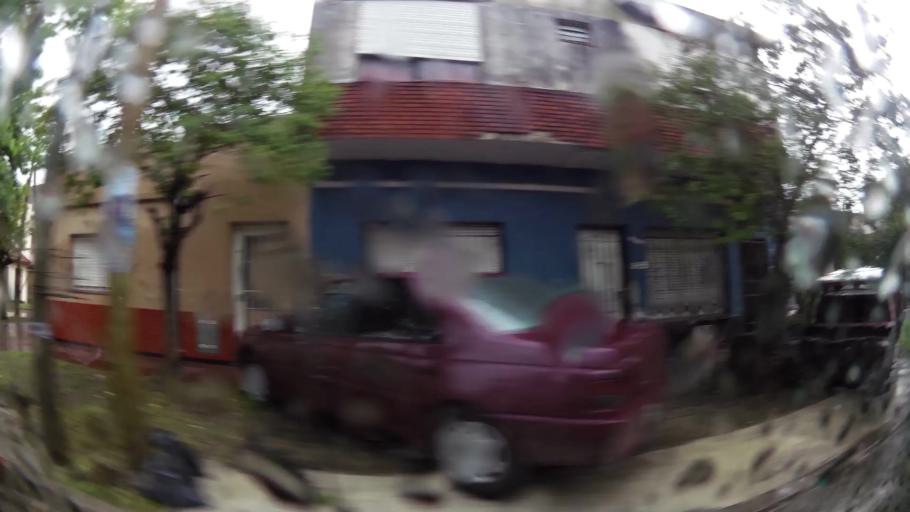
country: AR
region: Buenos Aires
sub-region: Partido de Lanus
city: Lanus
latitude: -34.7165
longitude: -58.4071
